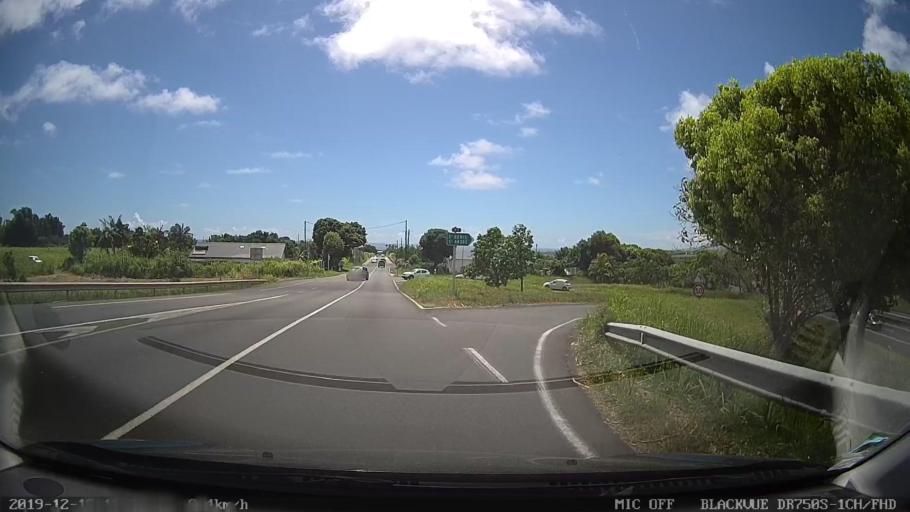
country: RE
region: Reunion
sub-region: Reunion
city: Bras-Panon
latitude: -20.9906
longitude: 55.6639
